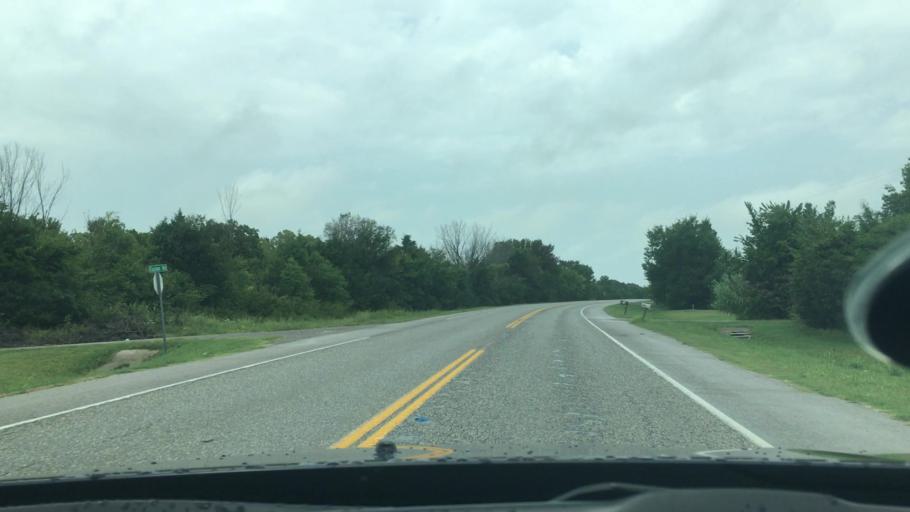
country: US
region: Oklahoma
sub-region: Johnston County
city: Tishomingo
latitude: 34.2478
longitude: -96.7570
